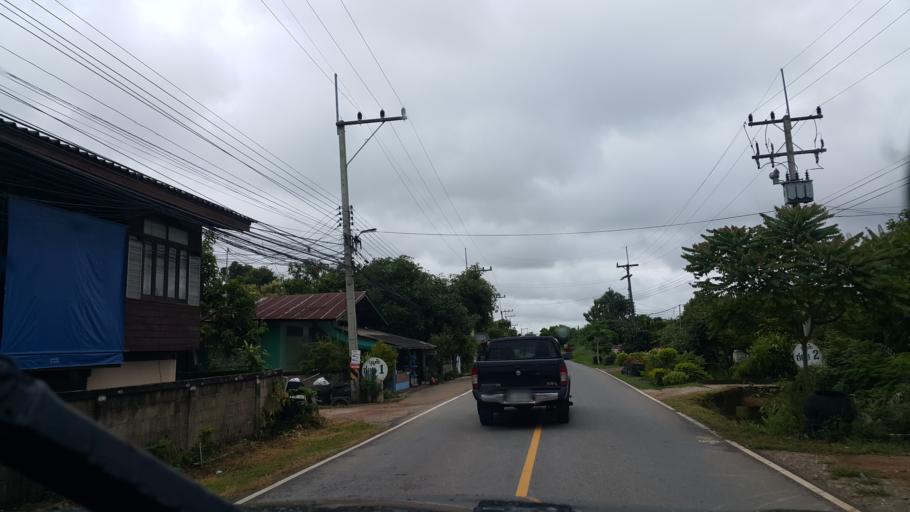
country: TH
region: Phayao
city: Chiang Kham
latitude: 19.5231
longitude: 100.3383
